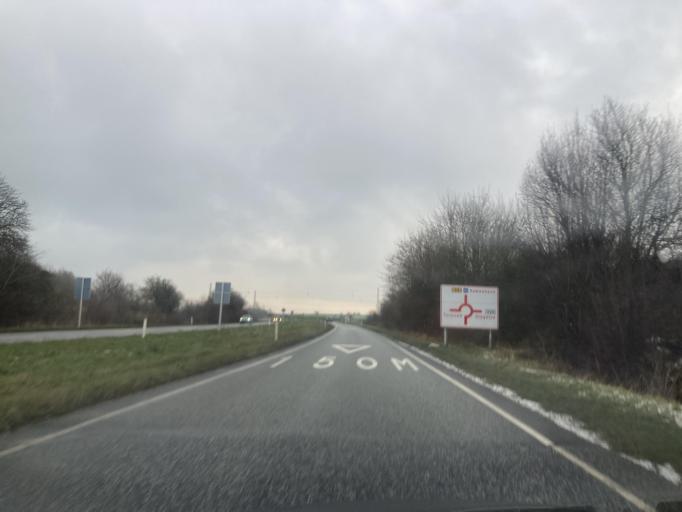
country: DK
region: Zealand
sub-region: Holbaek Kommune
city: Jyderup
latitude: 55.6514
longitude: 11.4338
